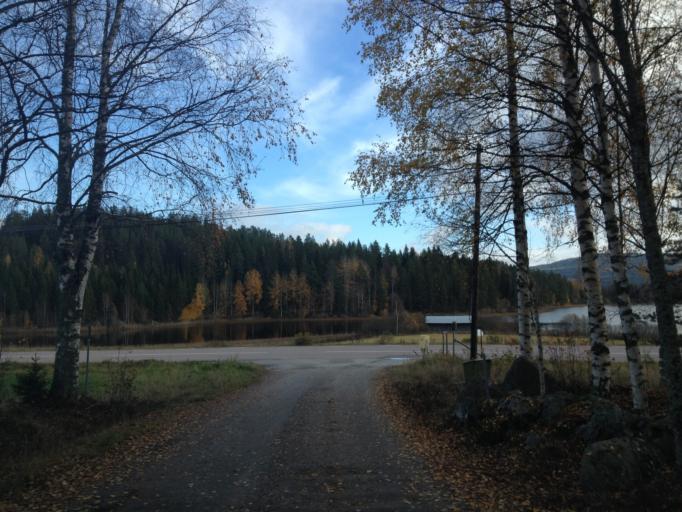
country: SE
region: Gaevleborg
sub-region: Bollnas Kommun
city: Kilafors
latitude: 61.2140
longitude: 16.4912
